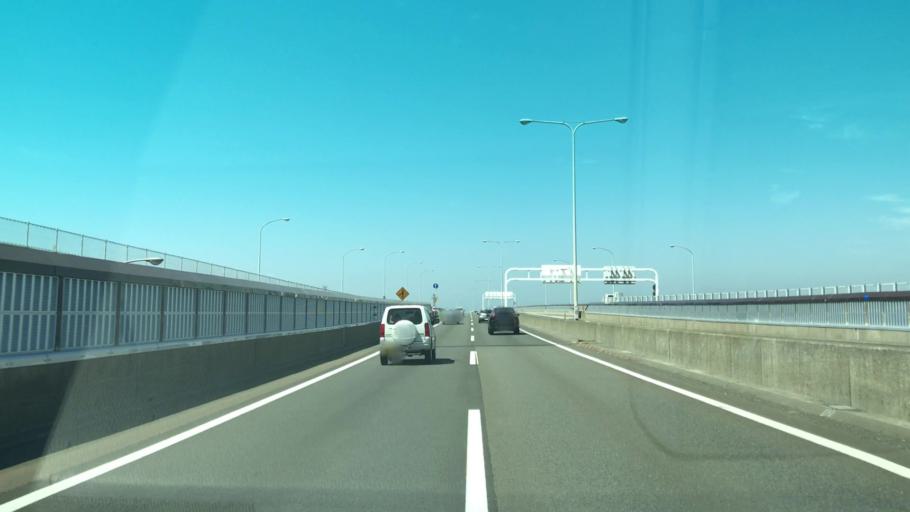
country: JP
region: Hokkaido
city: Sapporo
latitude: 43.0781
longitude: 141.4202
